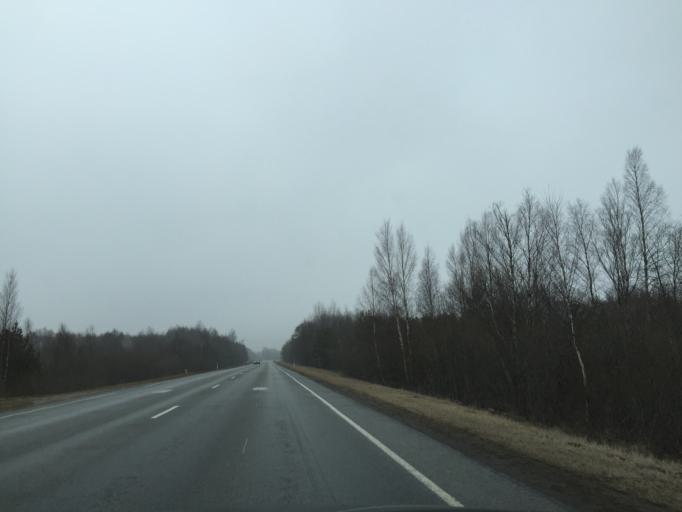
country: EE
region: Laeaene
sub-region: Lihula vald
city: Lihula
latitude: 58.5954
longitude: 23.5460
